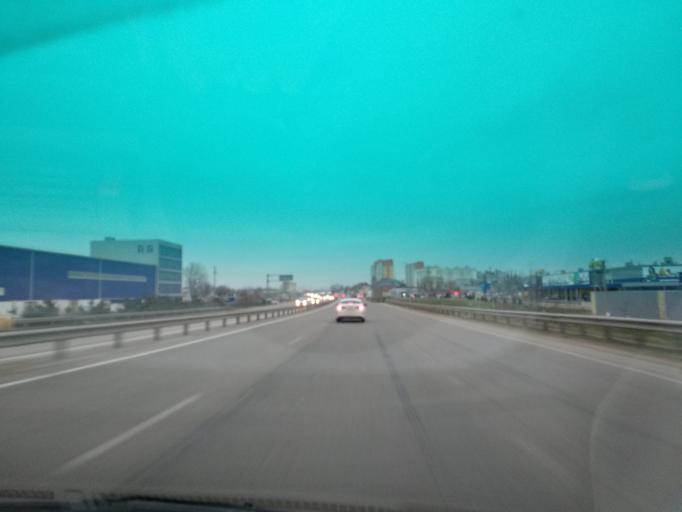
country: RU
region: Krasnodarskiy
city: Pashkovskiy
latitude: 45.0398
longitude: 39.1281
